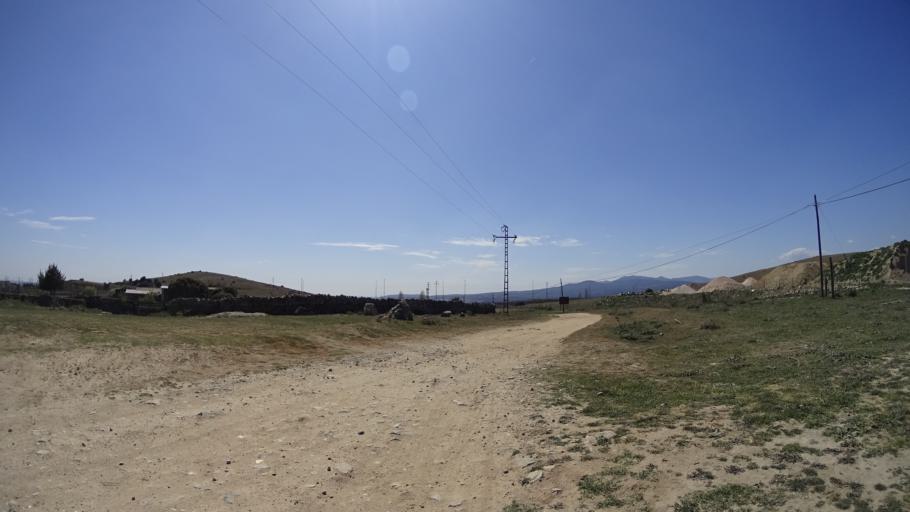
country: ES
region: Madrid
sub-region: Provincia de Madrid
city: Colmenar Viejo
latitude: 40.6843
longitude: -3.7742
